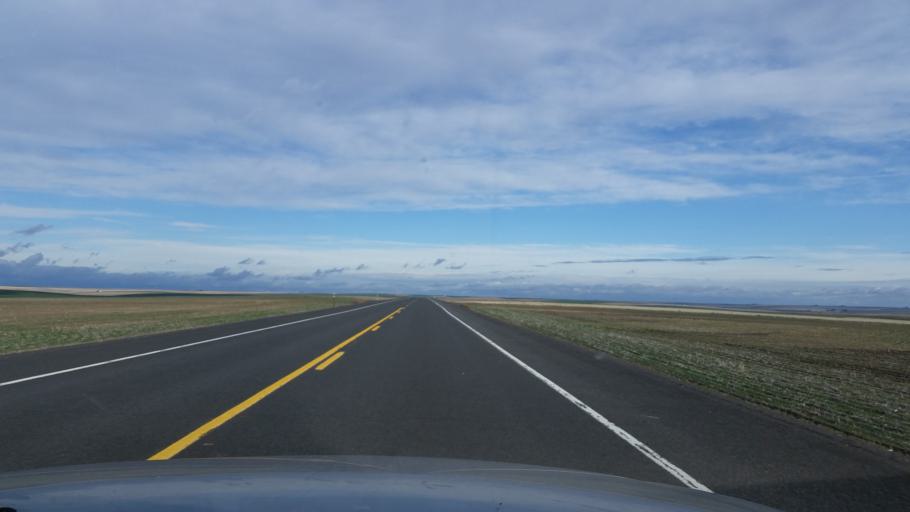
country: US
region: Washington
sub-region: Adams County
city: Ritzville
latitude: 47.3836
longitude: -118.4248
